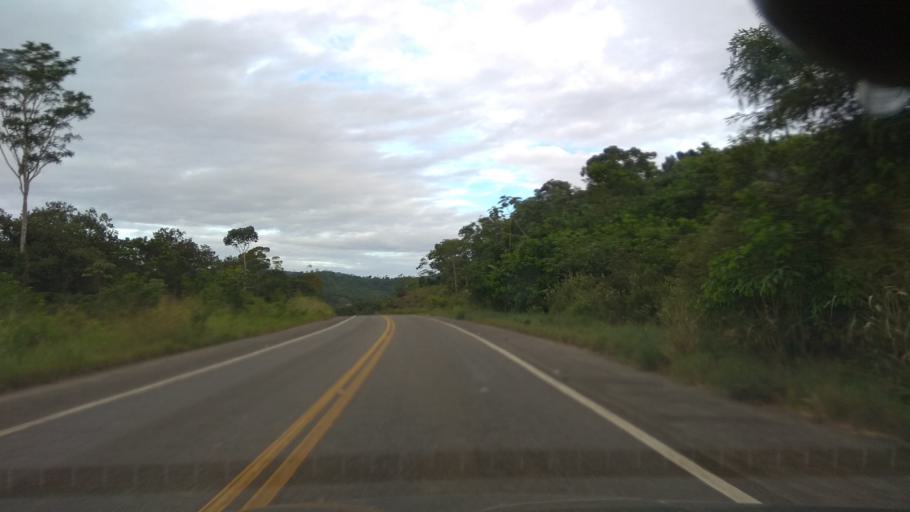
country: BR
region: Bahia
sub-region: Ibirapitanga
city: Ibirapitanga
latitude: -14.2425
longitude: -39.3823
